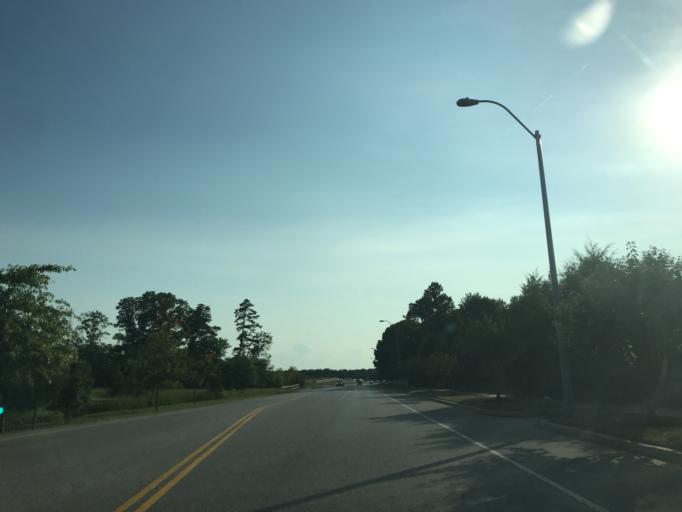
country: US
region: Maryland
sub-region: Anne Arundel County
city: South Gate
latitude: 39.1048
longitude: -76.6208
